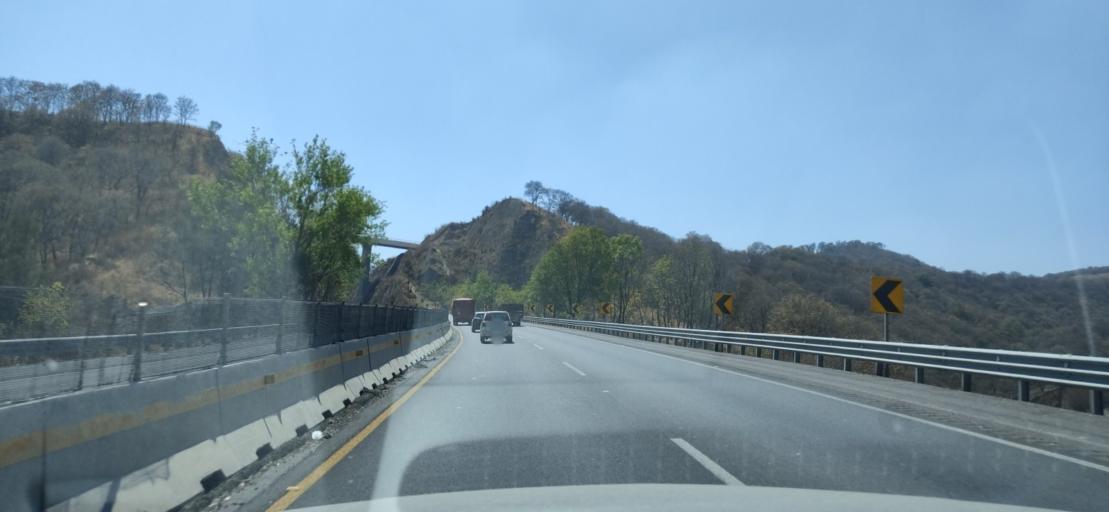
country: MX
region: Mexico
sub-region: Naucalpan de Juarez
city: La Rosa
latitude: 19.4797
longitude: -99.3130
